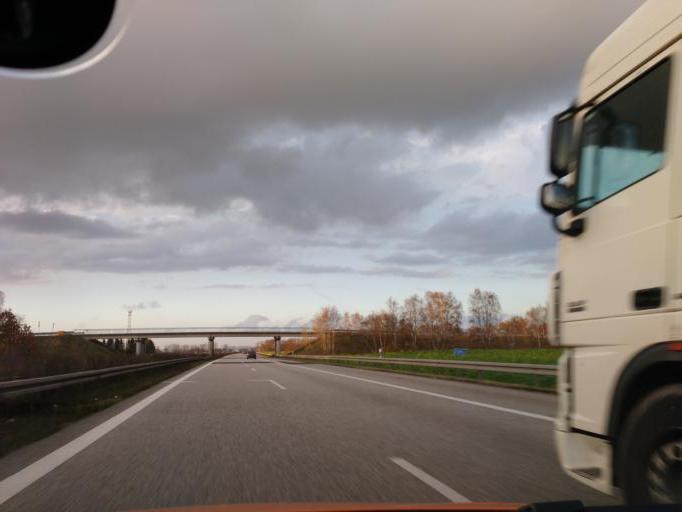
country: DE
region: Mecklenburg-Vorpommern
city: Neustadt-Glewe
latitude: 53.4017
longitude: 11.5768
